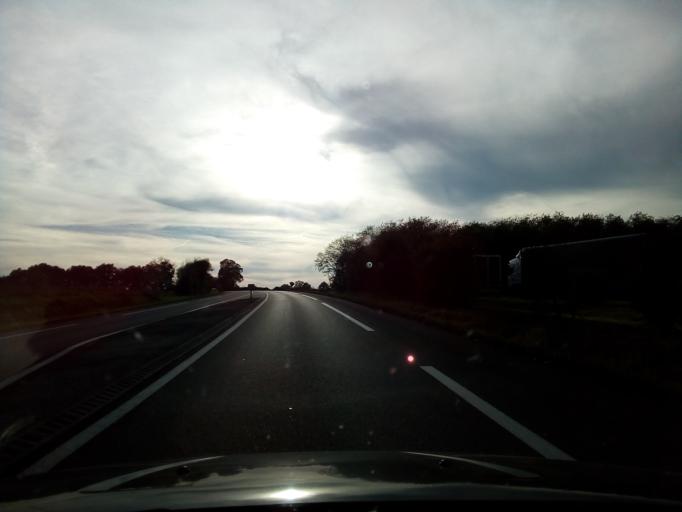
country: FR
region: Poitou-Charentes
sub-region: Departement de la Charente
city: Saint-Claud
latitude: 45.9137
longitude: 0.4954
